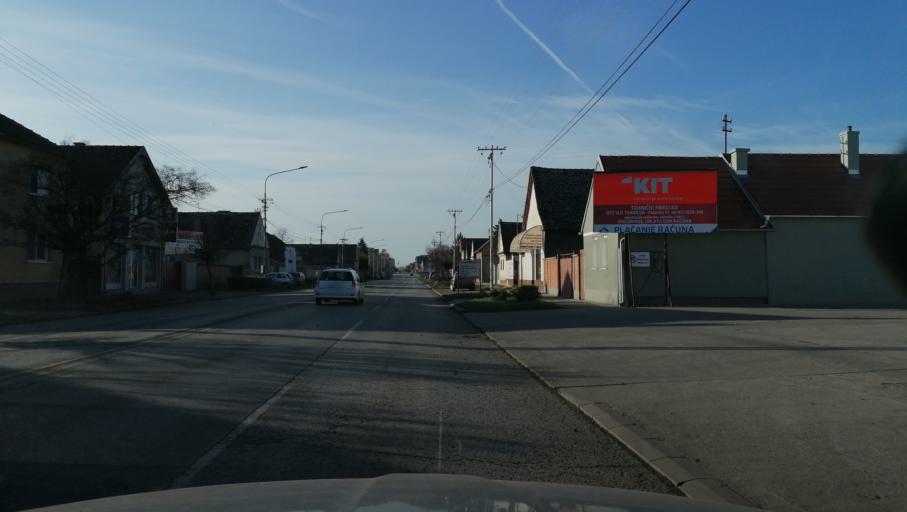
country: RS
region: Autonomna Pokrajina Vojvodina
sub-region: Sremski Okrug
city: Sremska Mitrovica
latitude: 44.9712
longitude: 19.6246
